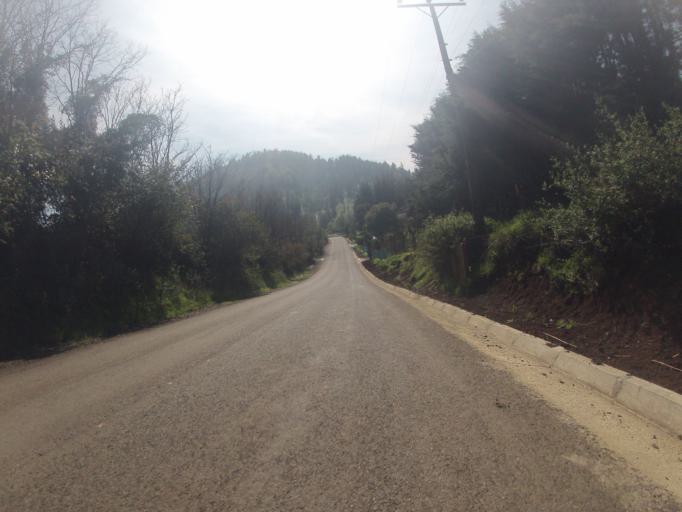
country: CL
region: Araucania
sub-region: Provincia de Cautin
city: Temuco
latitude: -38.7068
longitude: -72.5954
